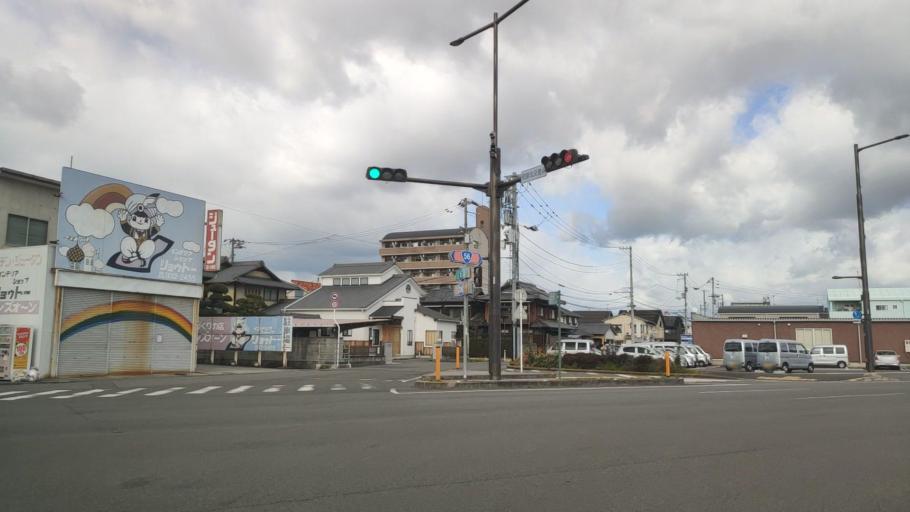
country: JP
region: Ehime
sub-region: Shikoku-chuo Shi
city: Matsuyama
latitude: 33.8233
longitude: 132.7574
